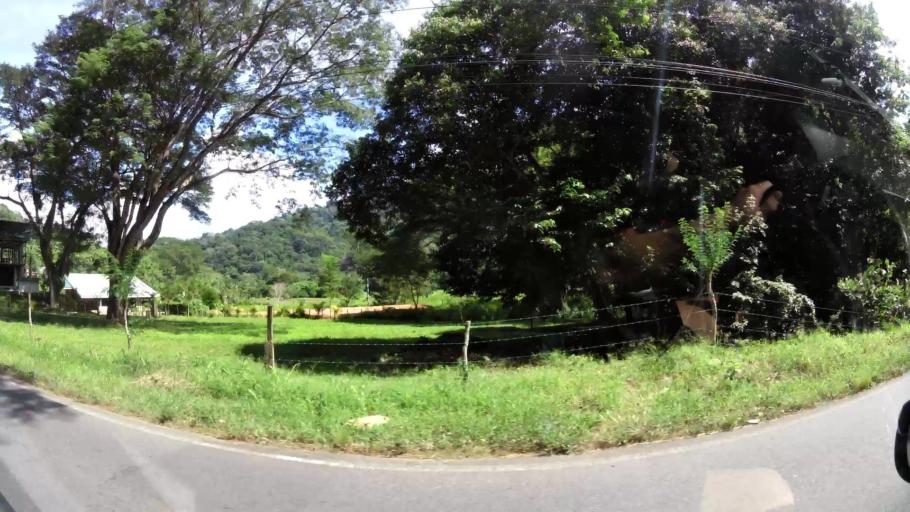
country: CR
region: San Jose
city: San Isidro
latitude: 9.2663
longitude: -83.8638
